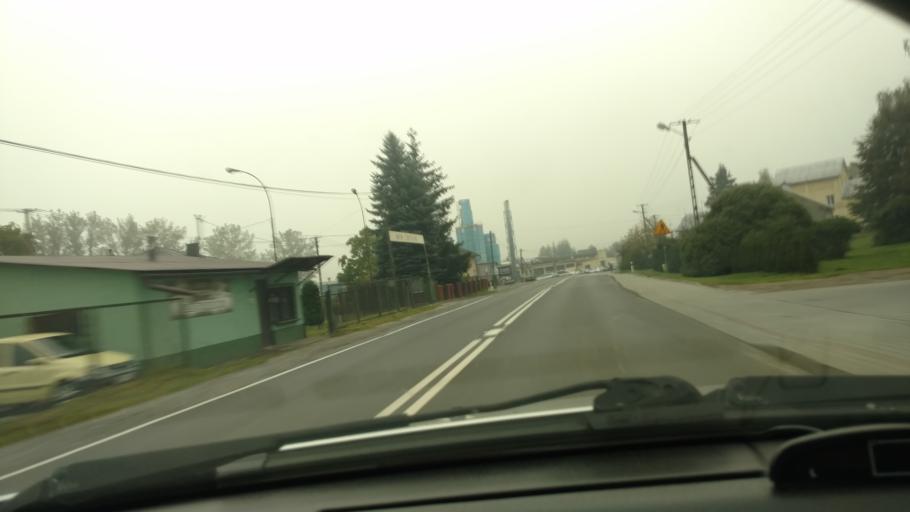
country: PL
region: Subcarpathian Voivodeship
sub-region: Powiat strzyzowski
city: Frysztak
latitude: 49.8307
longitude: 21.6167
